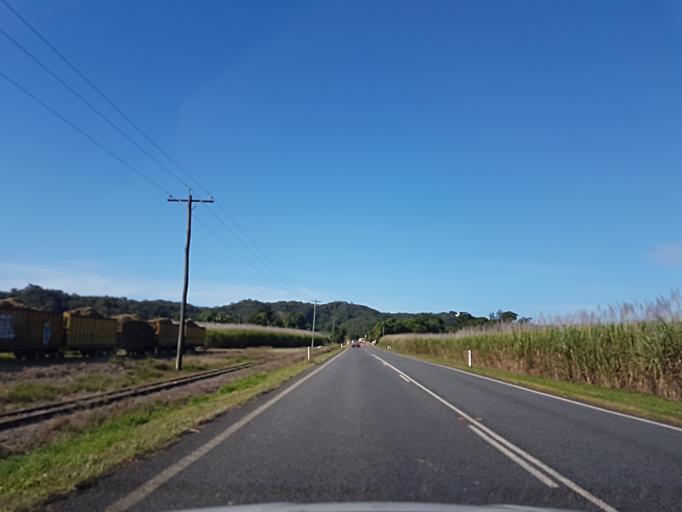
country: AU
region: Queensland
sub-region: Cairns
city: Port Douglas
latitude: -16.3928
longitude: 145.3905
